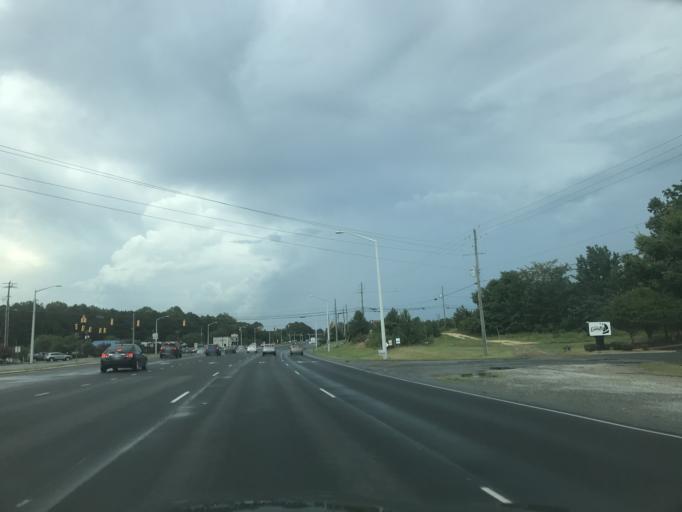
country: US
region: North Carolina
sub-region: Johnston County
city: Clayton
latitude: 35.6425
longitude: -78.4526
